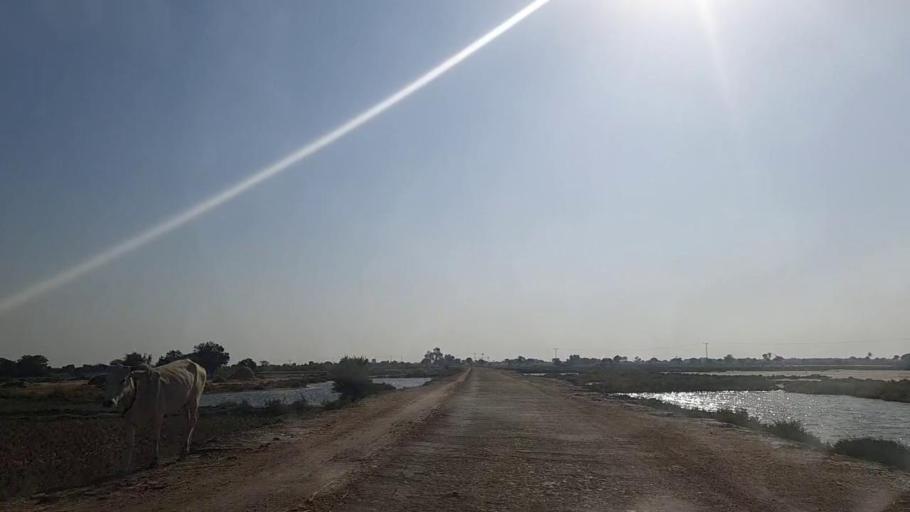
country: PK
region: Sindh
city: Mirpur Batoro
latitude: 24.6016
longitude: 68.1716
